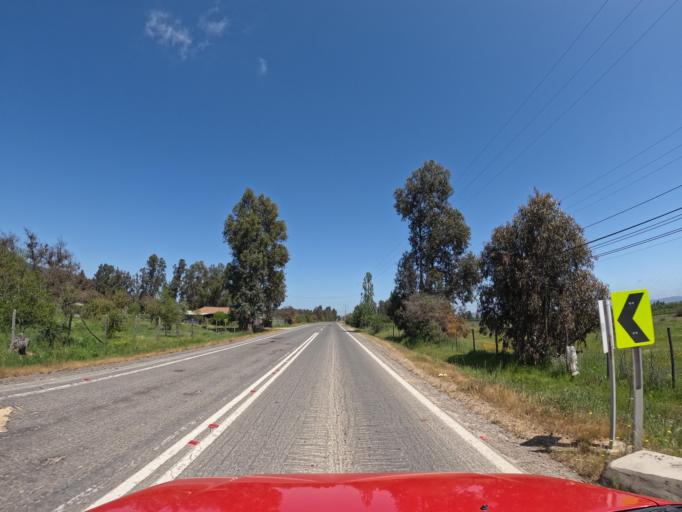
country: CL
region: O'Higgins
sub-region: Provincia de Colchagua
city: Santa Cruz
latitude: -34.7312
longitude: -71.6789
